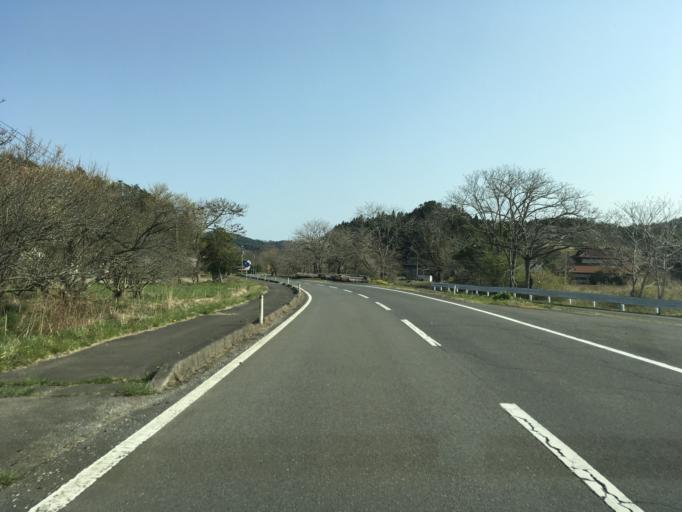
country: JP
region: Iwate
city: Ichinoseki
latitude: 38.7868
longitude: 141.3239
